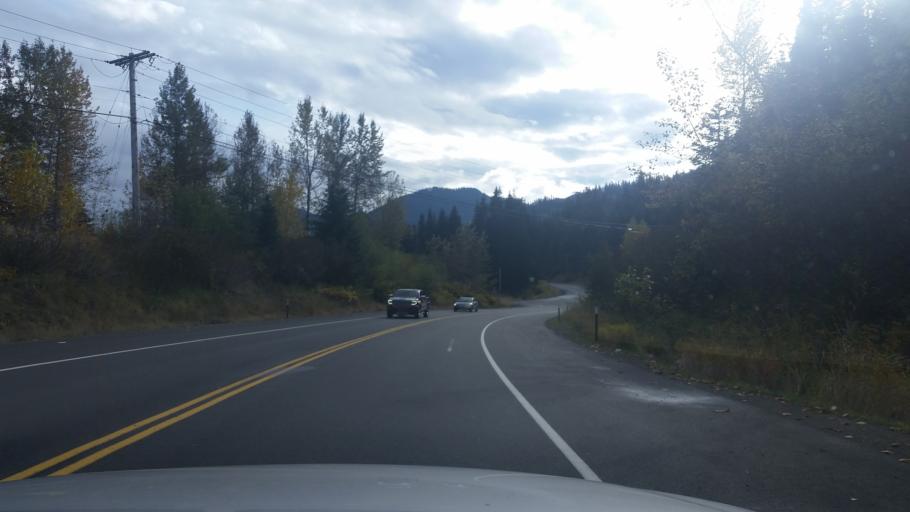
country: US
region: Washington
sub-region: King County
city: Tanner
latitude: 47.4203
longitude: -121.4118
